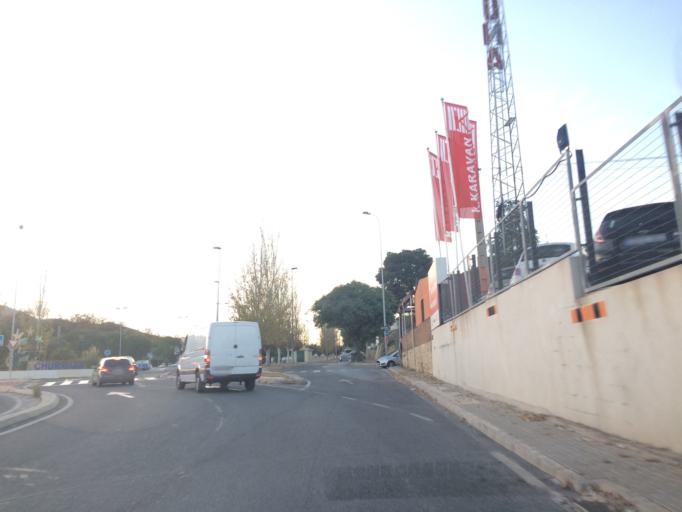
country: ES
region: Andalusia
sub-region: Provincia de Malaga
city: Torremolinos
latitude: 36.6578
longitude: -4.4866
